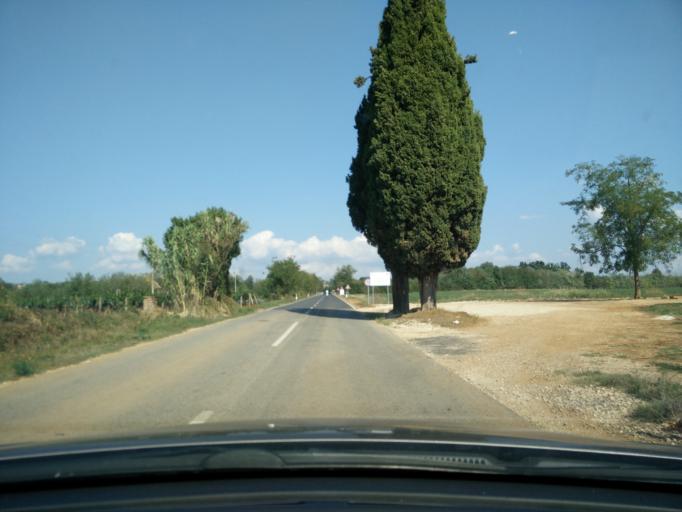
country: HR
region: Istarska
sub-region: Grad Porec
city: Porec
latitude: 45.2843
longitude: 13.6696
